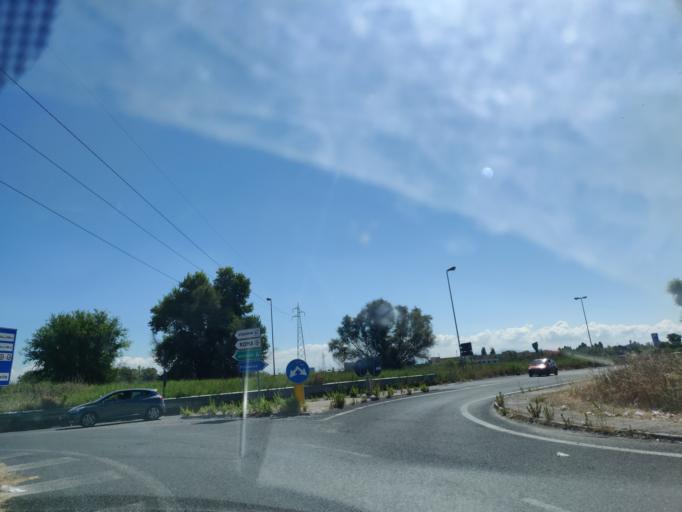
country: IT
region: Latium
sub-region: Citta metropolitana di Roma Capitale
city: Npp 23 (Parco Leonardo)
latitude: 41.8075
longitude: 12.3065
